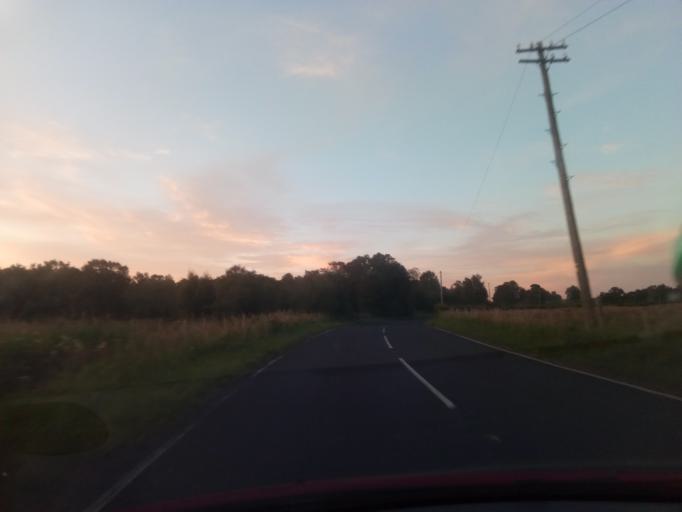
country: GB
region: England
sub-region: Northumberland
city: Bardon Mill
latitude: 54.9443
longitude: -2.2857
